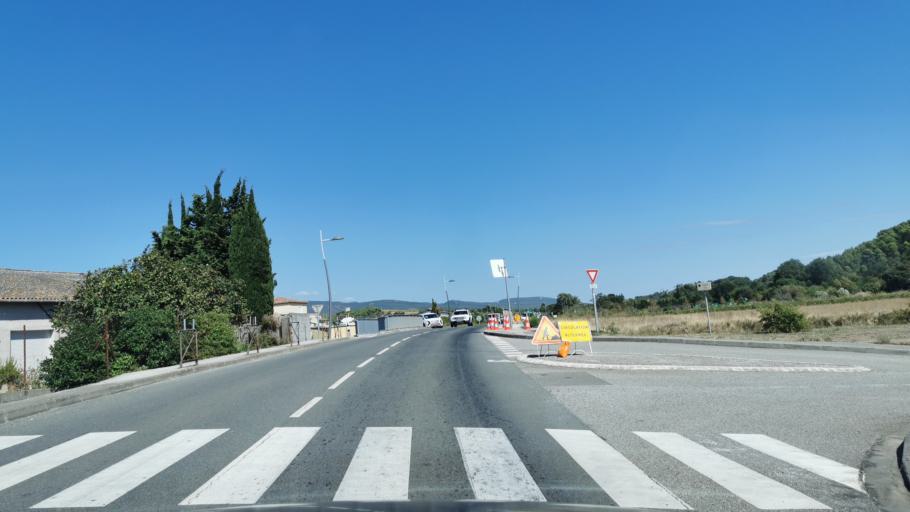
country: FR
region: Languedoc-Roussillon
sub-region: Departement de l'Aude
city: Conques-sur-Orbiel
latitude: 43.2890
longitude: 2.4422
